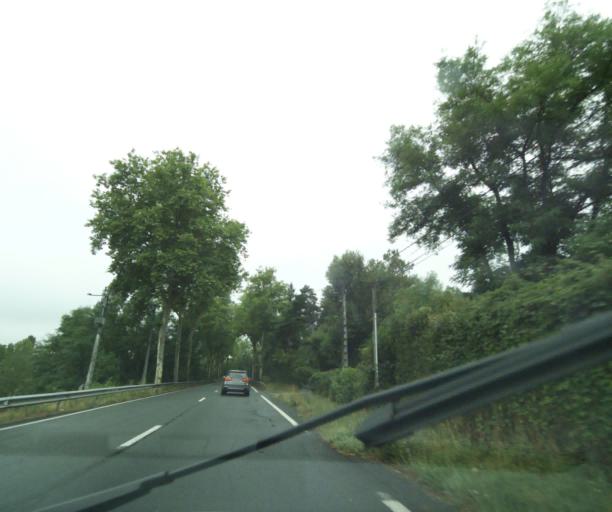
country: FR
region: Midi-Pyrenees
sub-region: Departement du Tarn
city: Le Garric
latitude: 43.9796
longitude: 2.1752
